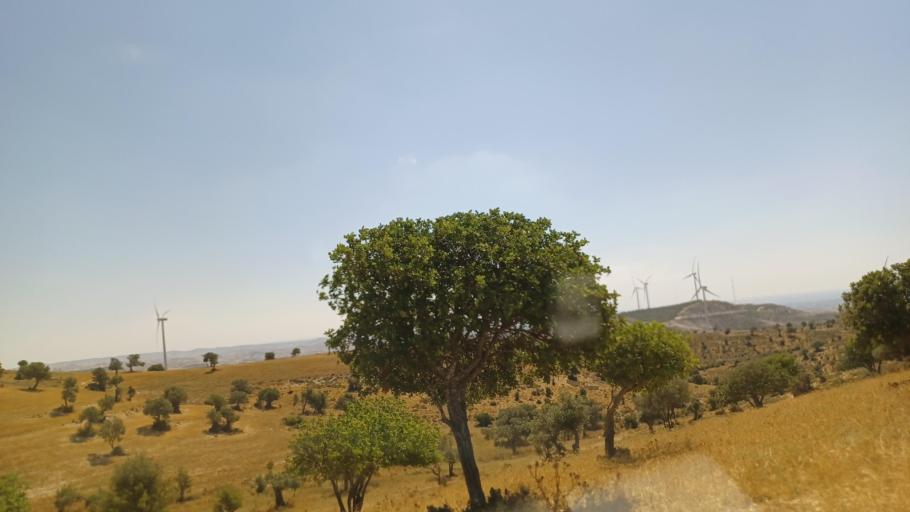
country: CY
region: Larnaka
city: Psevdas
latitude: 34.9599
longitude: 33.4828
